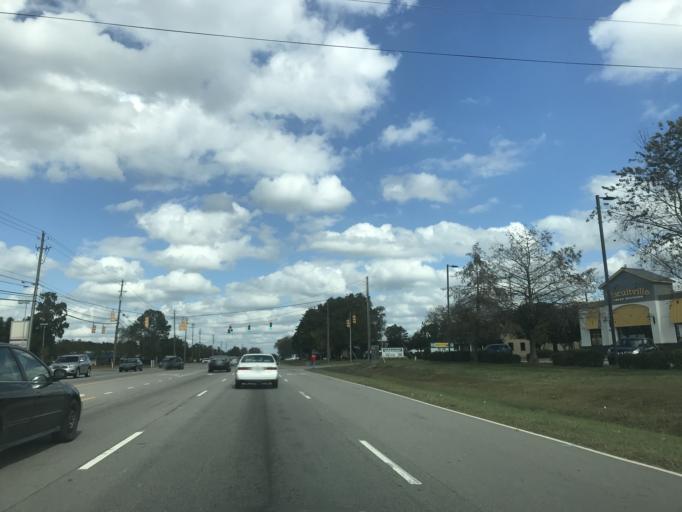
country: US
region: North Carolina
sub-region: Wake County
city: Garner
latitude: 35.7202
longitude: -78.6538
